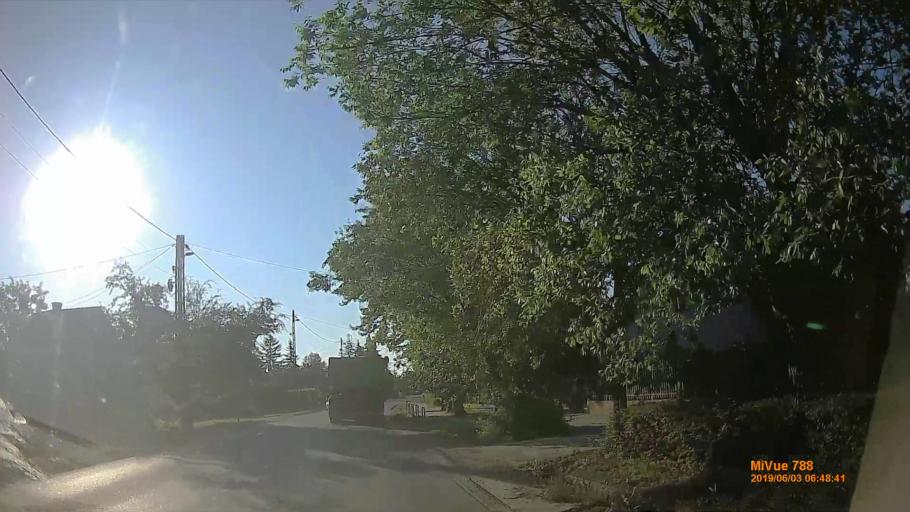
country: HU
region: Pest
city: Bugyi
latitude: 47.2225
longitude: 19.1573
